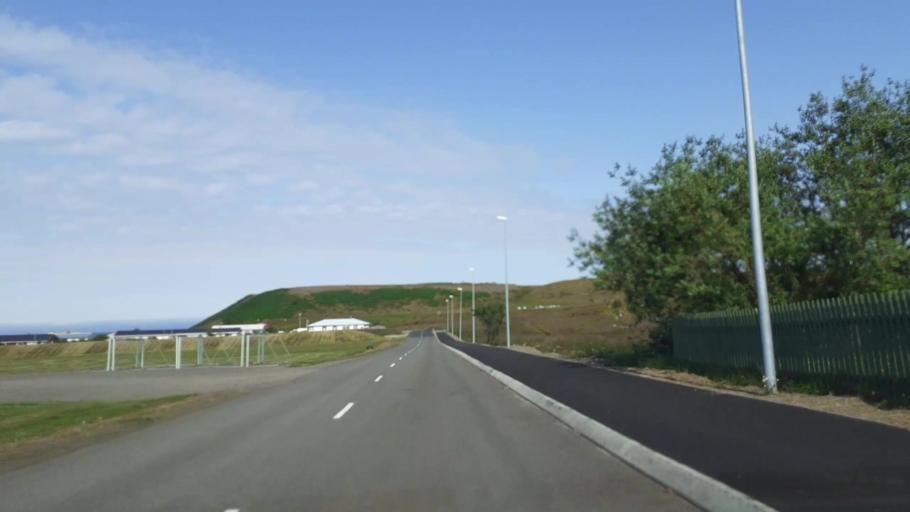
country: IS
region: Northwest
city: Saudarkrokur
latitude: 65.6626
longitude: -20.2827
